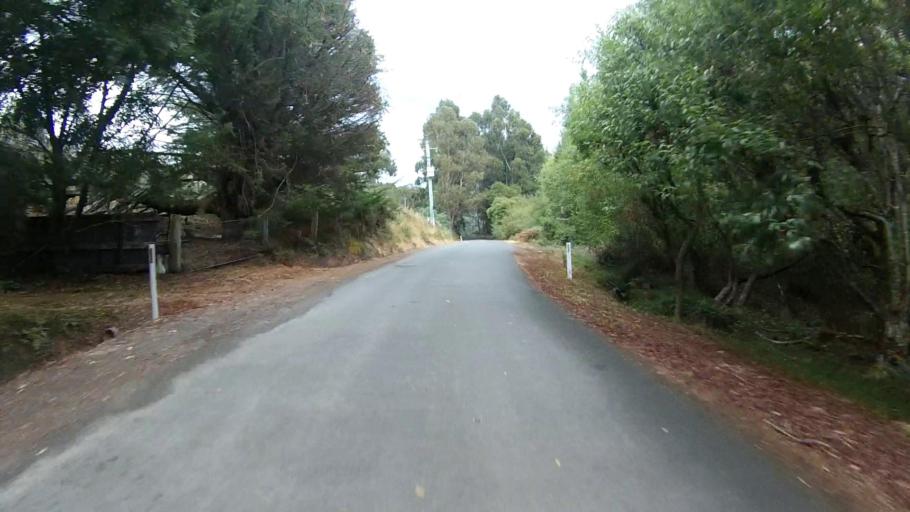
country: AU
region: Tasmania
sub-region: Huon Valley
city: Cygnet
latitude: -43.2333
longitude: 147.1583
